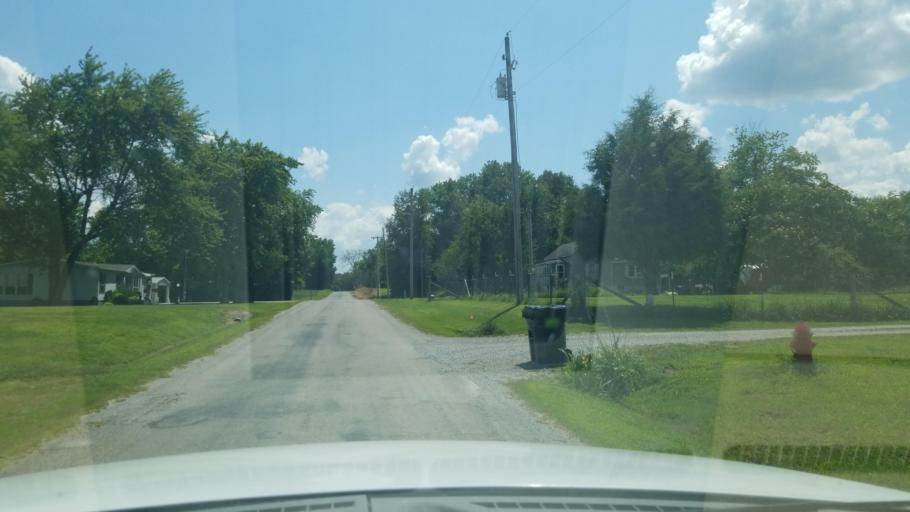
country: US
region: Illinois
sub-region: Saline County
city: Harrisburg
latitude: 37.7701
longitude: -88.5171
